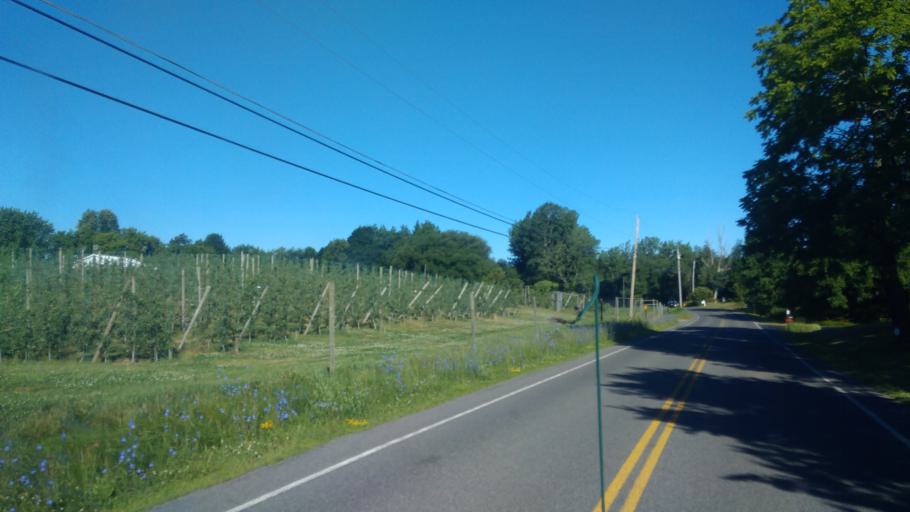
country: US
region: New York
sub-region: Wayne County
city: Williamson
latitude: 43.2828
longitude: -77.1343
